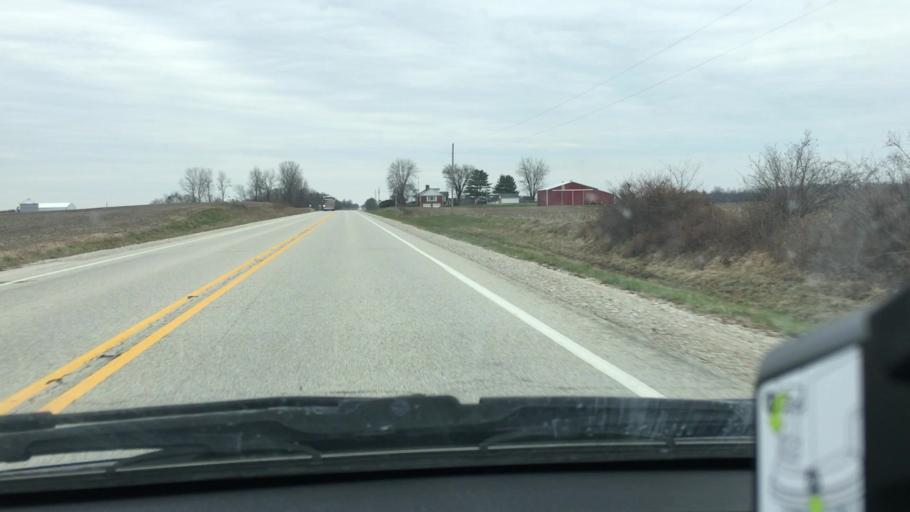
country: US
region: Indiana
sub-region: Daviess County
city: Odon
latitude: 38.9413
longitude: -87.0168
